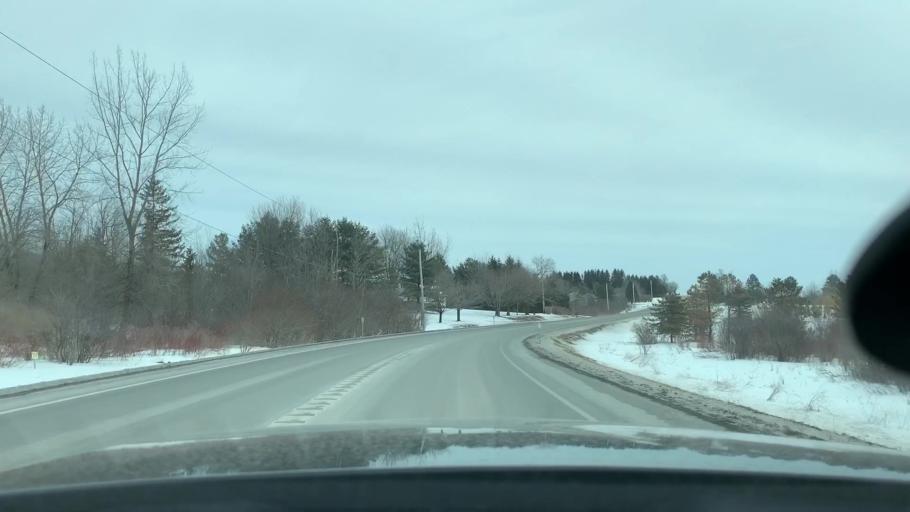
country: US
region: New York
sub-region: Oneida County
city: Utica
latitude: 43.0331
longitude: -75.1793
